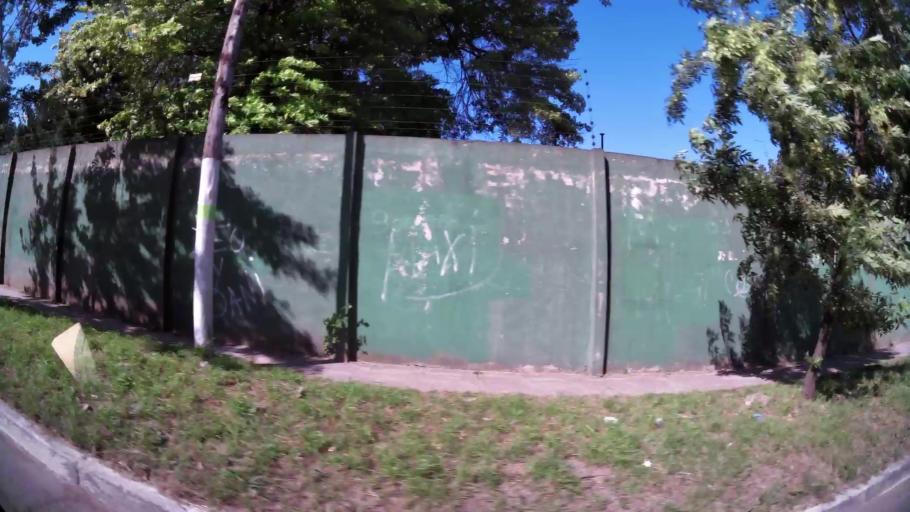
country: AR
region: Buenos Aires
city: Santa Catalina - Dique Lujan
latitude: -34.4739
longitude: -58.7060
